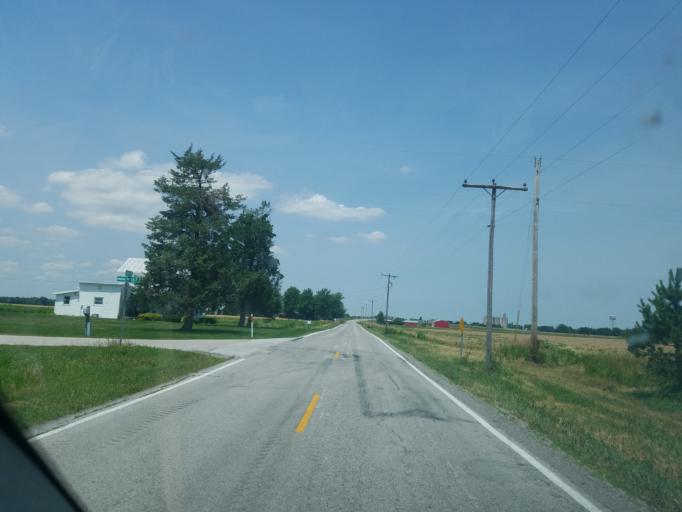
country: US
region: Ohio
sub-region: Wyandot County
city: Carey
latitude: 40.9627
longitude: -83.4860
